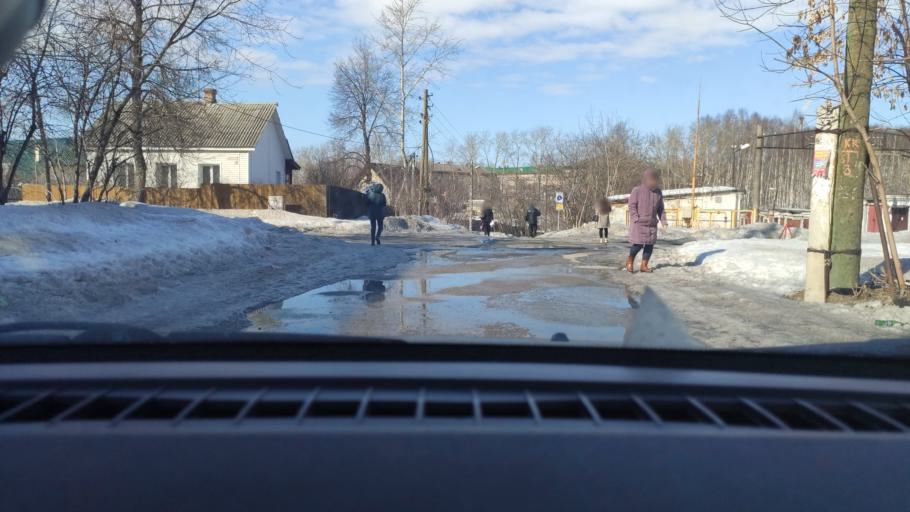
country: RU
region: Perm
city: Polazna
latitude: 58.1280
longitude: 56.3839
